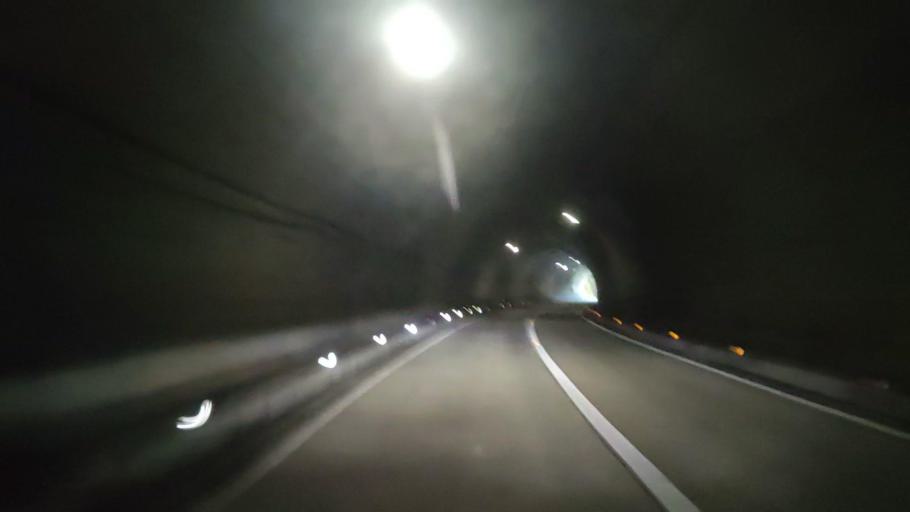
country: JP
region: Wakayama
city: Shingu
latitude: 33.8082
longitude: 135.7248
